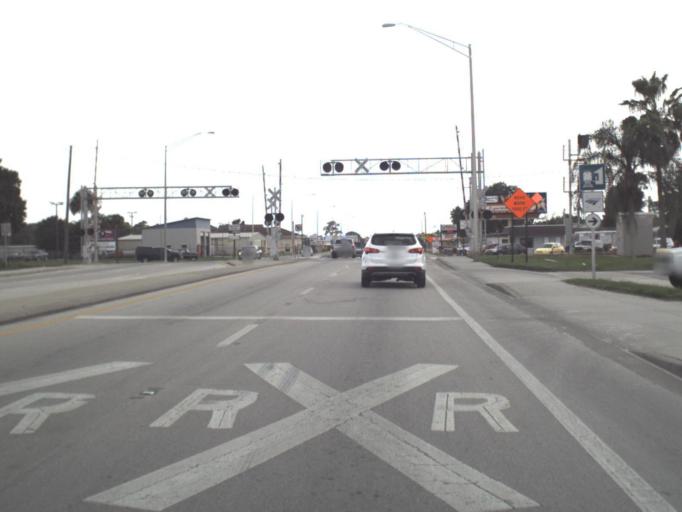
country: US
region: Florida
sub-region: Okeechobee County
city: Okeechobee
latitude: 27.2525
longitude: -80.8300
